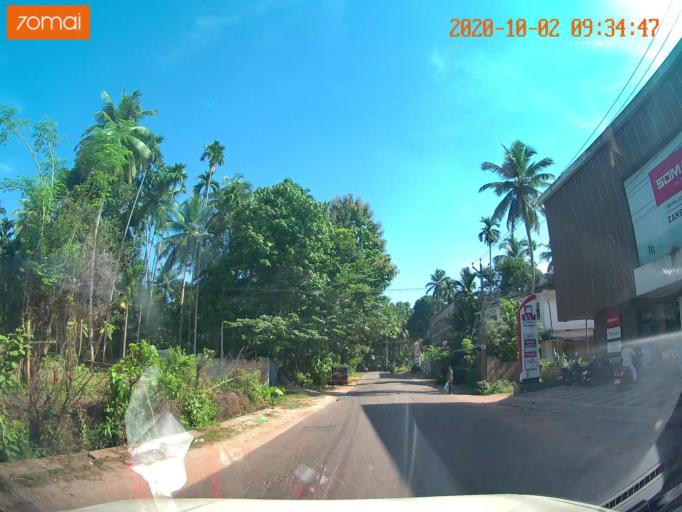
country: IN
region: Kerala
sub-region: Kozhikode
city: Nadapuram
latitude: 11.6402
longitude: 75.7549
